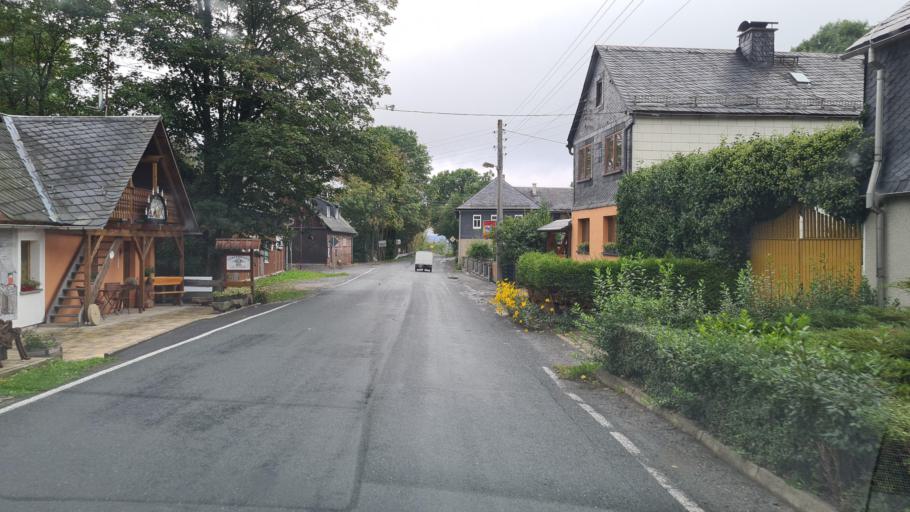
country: DE
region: Thuringia
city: Wurzbach
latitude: 50.5287
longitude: 11.5296
